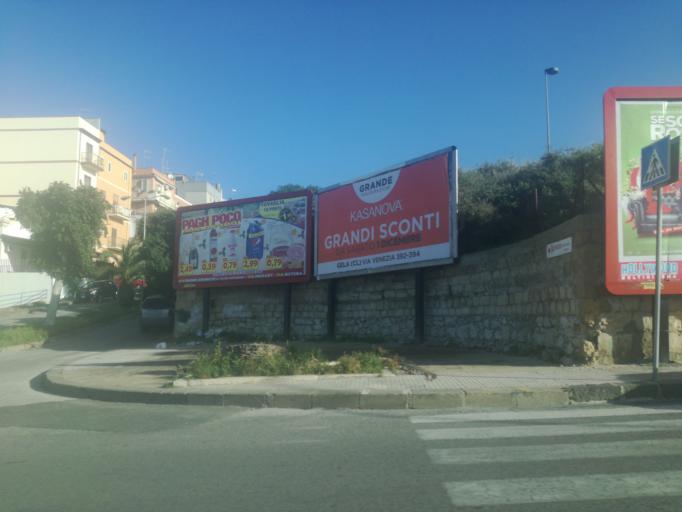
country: IT
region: Sicily
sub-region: Provincia di Caltanissetta
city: Gela
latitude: 37.0626
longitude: 14.2523
